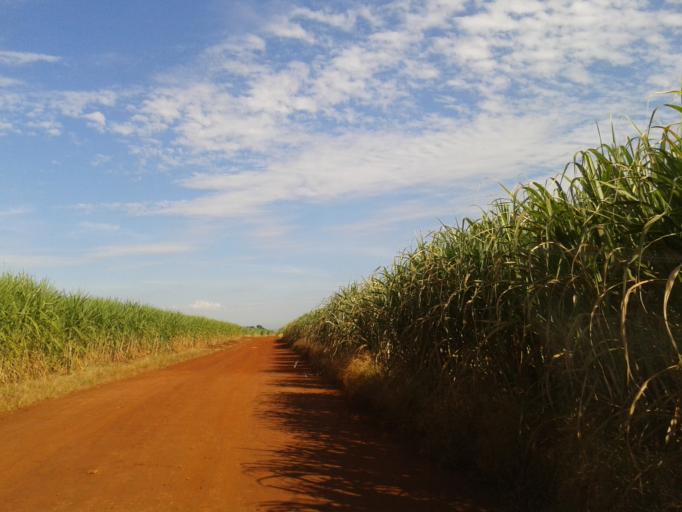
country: BR
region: Minas Gerais
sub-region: Centralina
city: Centralina
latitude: -18.6403
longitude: -49.2443
